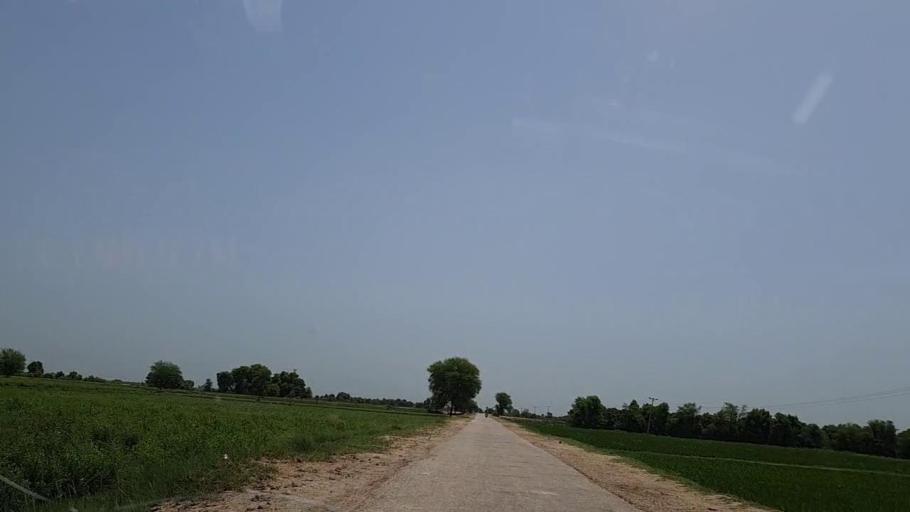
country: PK
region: Sindh
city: Tharu Shah
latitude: 26.9578
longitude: 68.0717
